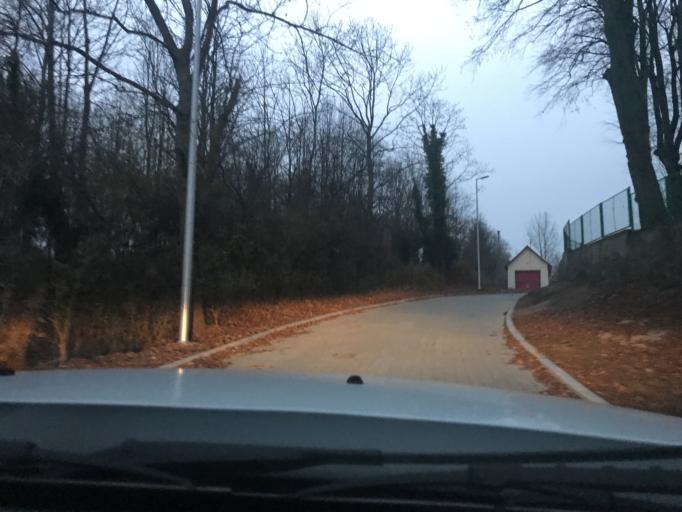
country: PL
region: West Pomeranian Voivodeship
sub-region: Powiat slawienski
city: Darlowo
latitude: 54.4780
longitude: 16.5115
